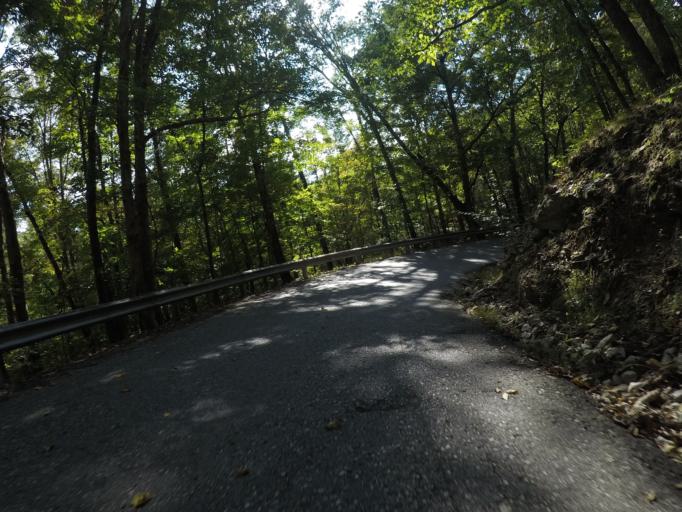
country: US
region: West Virginia
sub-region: Wayne County
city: Lavalette
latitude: 38.3677
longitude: -82.4778
